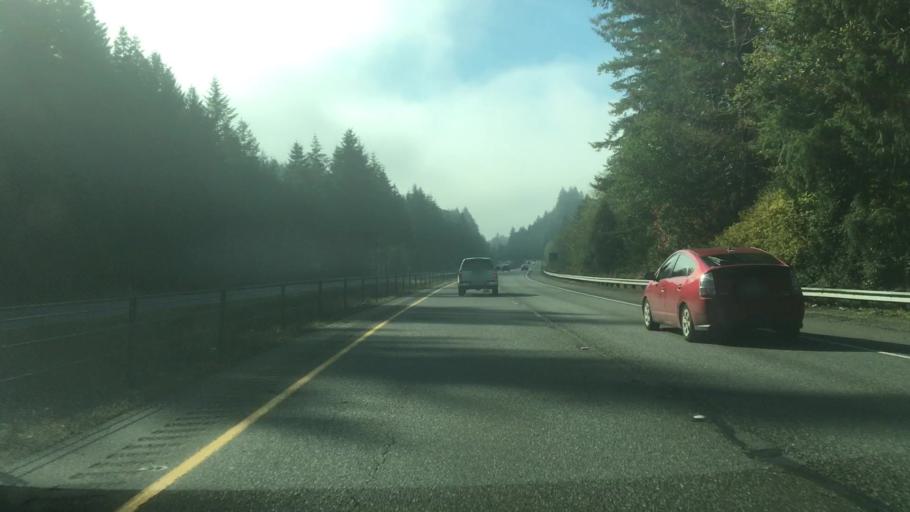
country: US
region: Washington
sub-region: Grays Harbor County
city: McCleary
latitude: 47.0410
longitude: -123.3223
